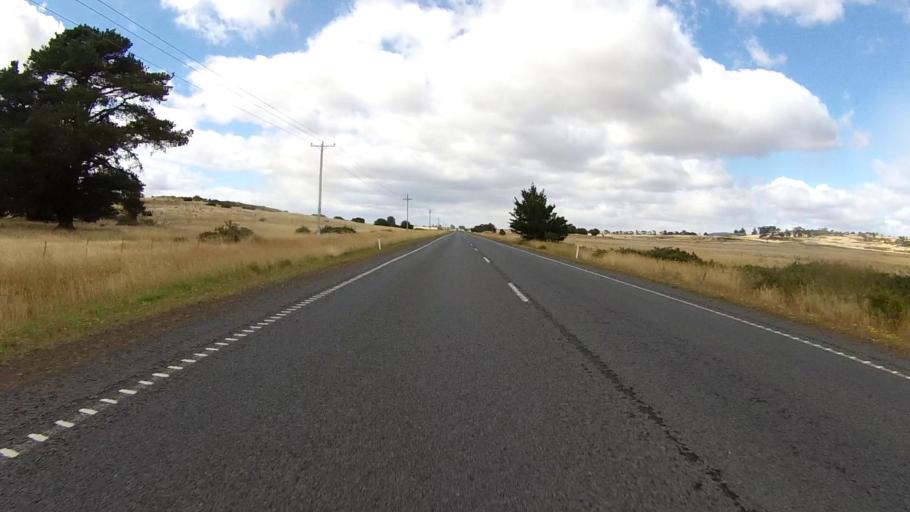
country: AU
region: Tasmania
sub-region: Northern Midlands
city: Evandale
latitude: -41.8486
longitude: 147.4502
